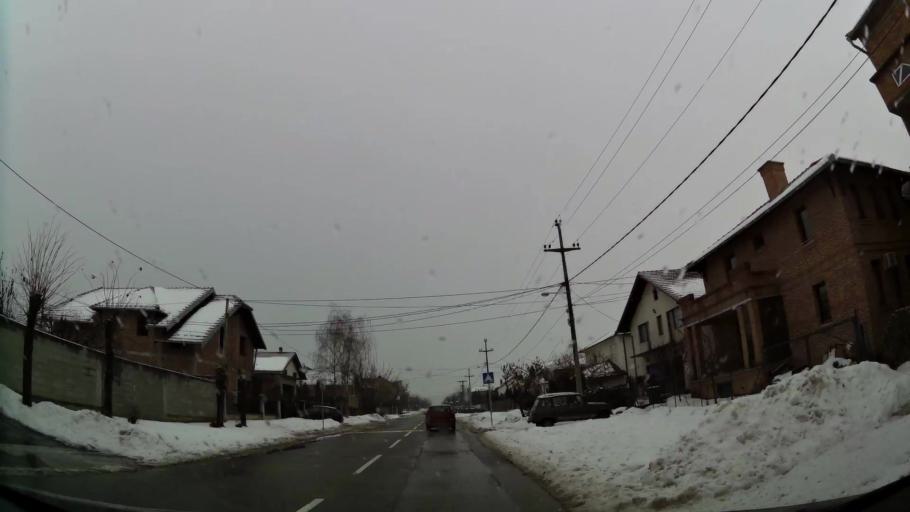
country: RS
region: Central Serbia
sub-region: Belgrade
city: Zemun
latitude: 44.8479
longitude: 20.3420
